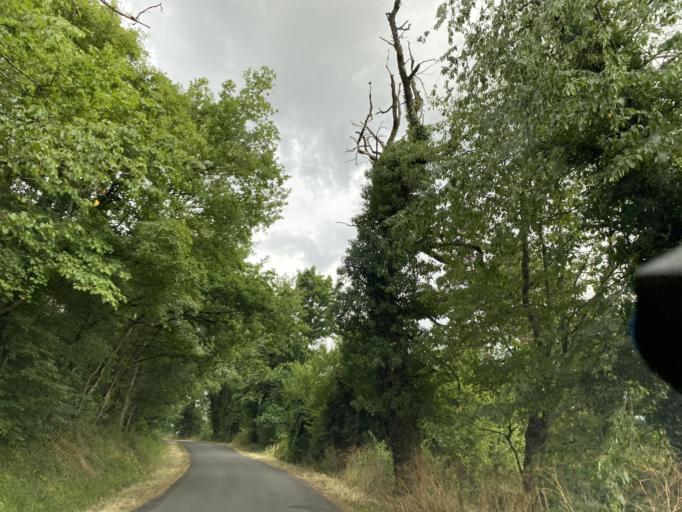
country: FR
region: Auvergne
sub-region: Departement du Puy-de-Dome
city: Peschadoires
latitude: 45.7554
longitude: 3.4513
